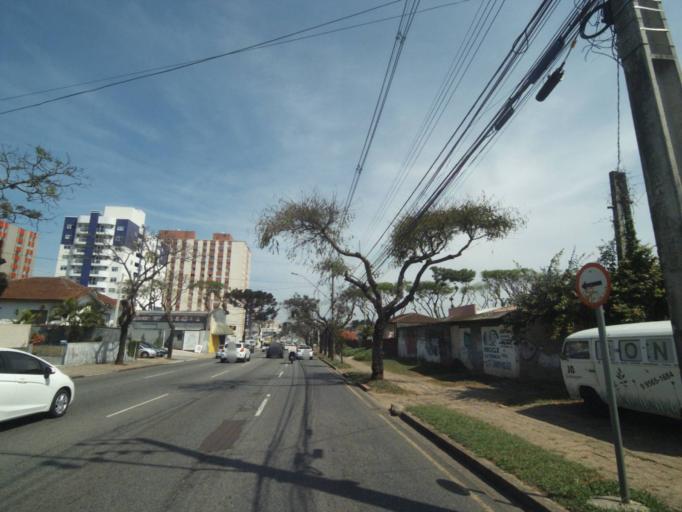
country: BR
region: Parana
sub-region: Curitiba
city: Curitiba
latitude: -25.4761
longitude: -49.2958
